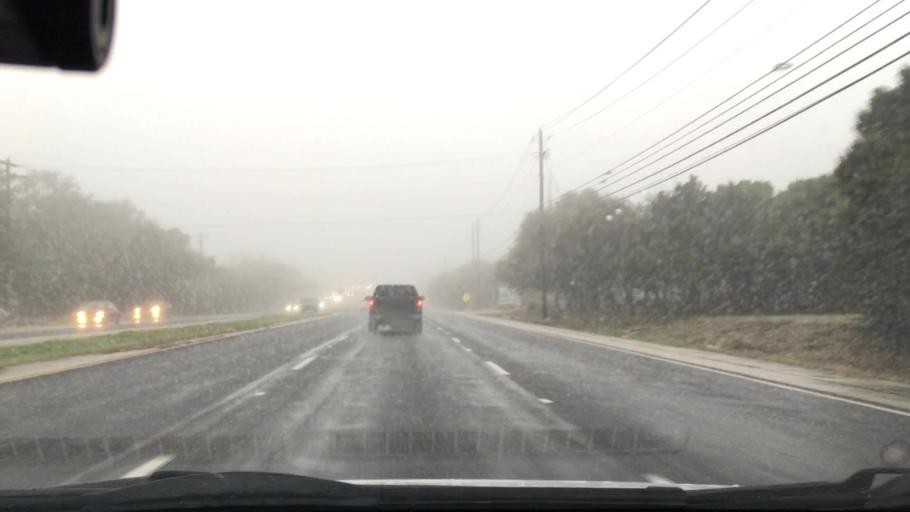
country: US
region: Texas
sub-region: Travis County
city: Barton Creek
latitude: 30.2460
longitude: -97.8455
